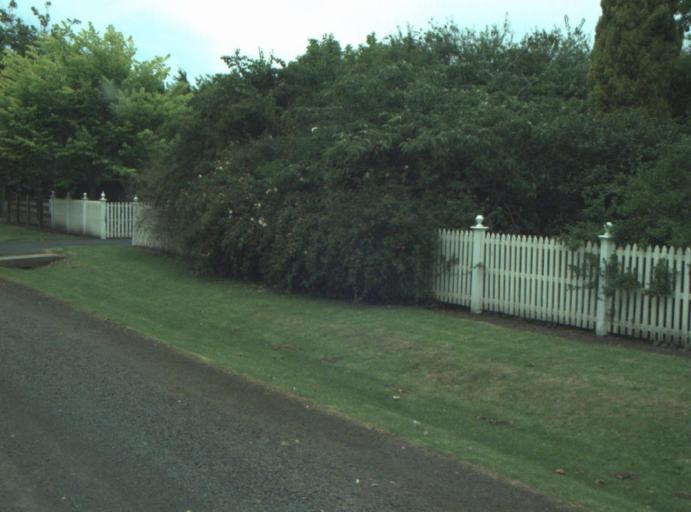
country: AU
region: Victoria
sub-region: Greater Geelong
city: Leopold
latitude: -38.2024
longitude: 144.4662
